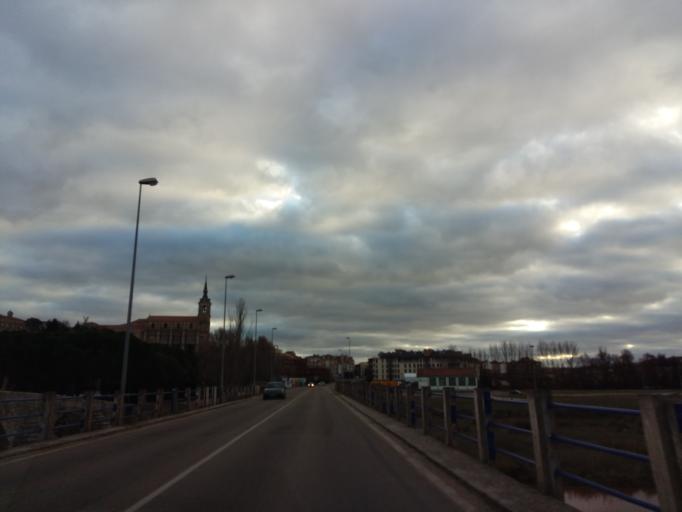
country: ES
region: Castille and Leon
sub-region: Provincia de Burgos
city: Lerma
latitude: 42.0306
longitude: -3.7590
